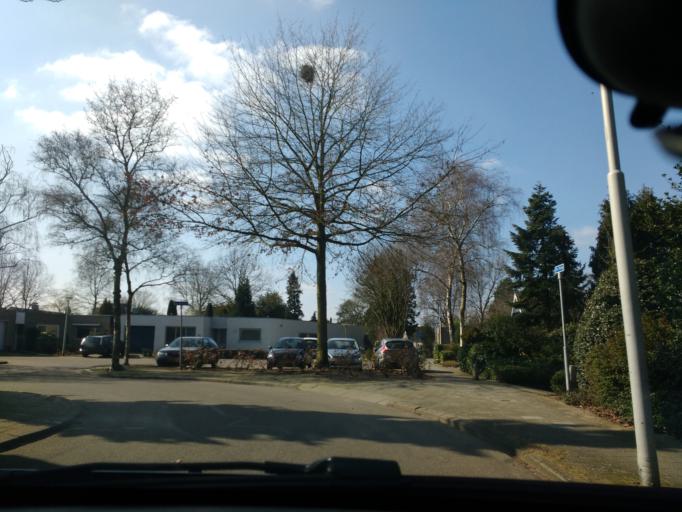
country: NL
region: Gelderland
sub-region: Gemeente Nijmegen
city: Nijmegen
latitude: 51.7895
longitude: 5.8516
